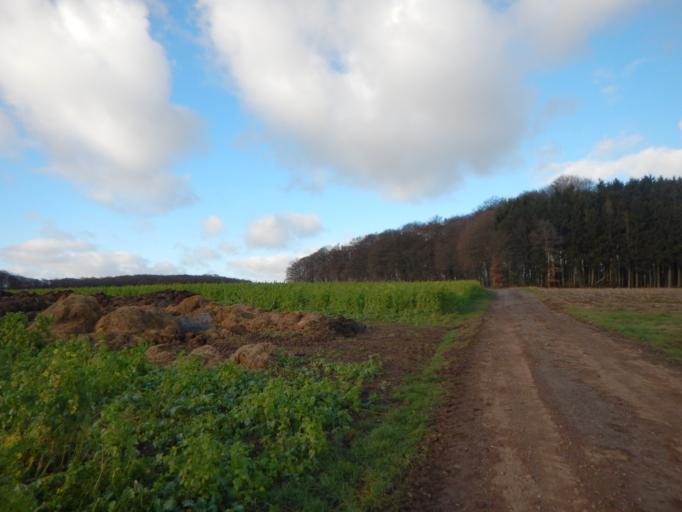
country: LU
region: Diekirch
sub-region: Canton de Redange
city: Redange-sur-Attert
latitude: 49.7716
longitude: 5.9128
